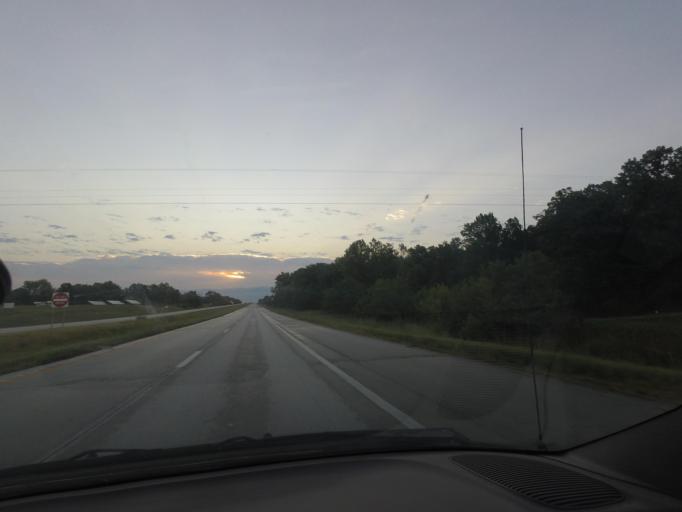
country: US
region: Missouri
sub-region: Macon County
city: Macon
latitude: 39.7554
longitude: -92.4535
